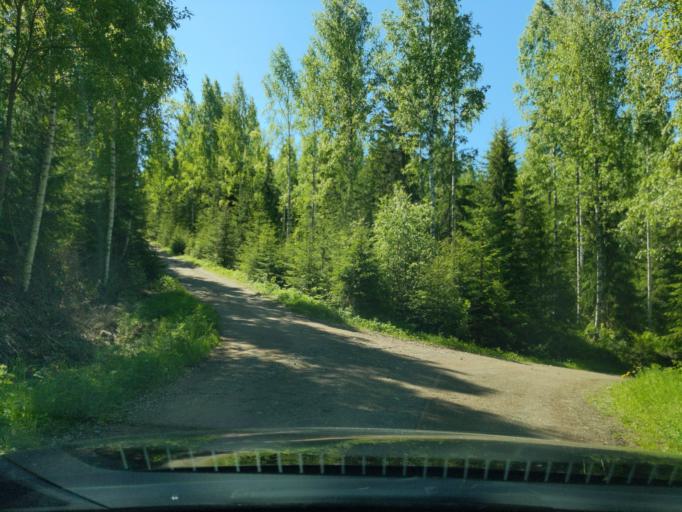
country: FI
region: Paijanne Tavastia
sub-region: Lahti
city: Lahti
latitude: 61.0540
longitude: 25.6961
